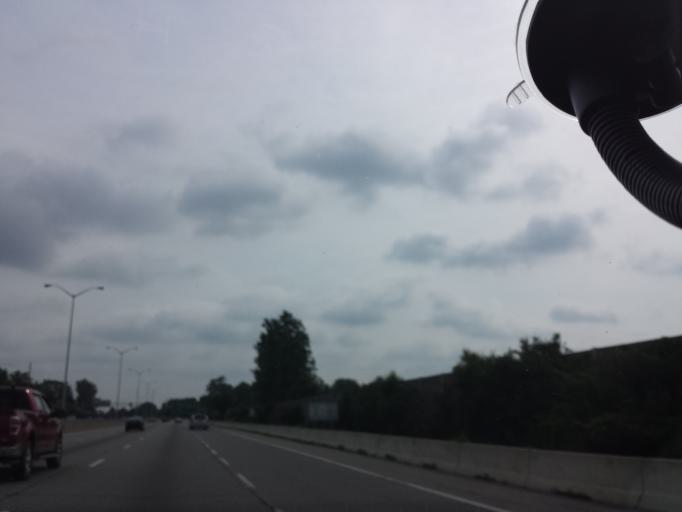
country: CA
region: Ontario
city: Ottawa
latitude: 45.3637
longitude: -75.7634
